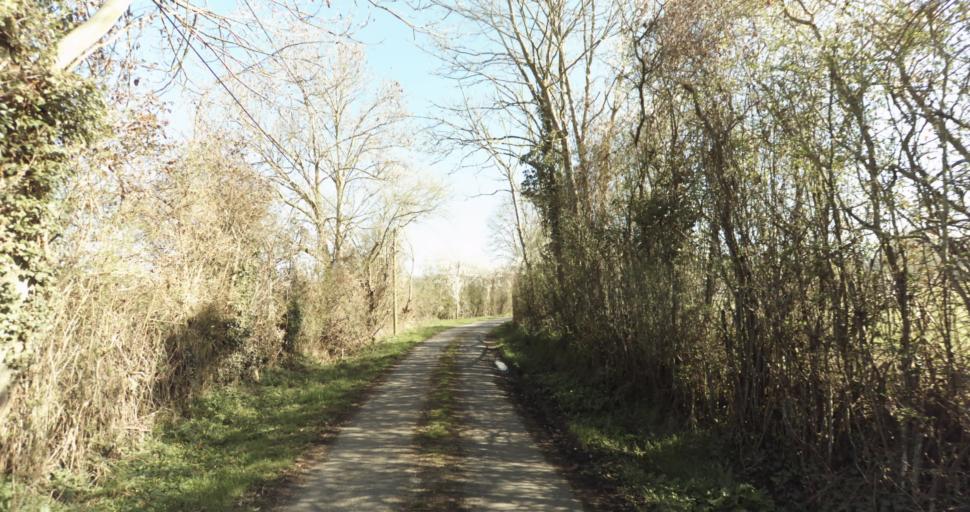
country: FR
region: Lower Normandy
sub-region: Departement du Calvados
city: Saint-Pierre-sur-Dives
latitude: 48.9719
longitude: 0.0345
